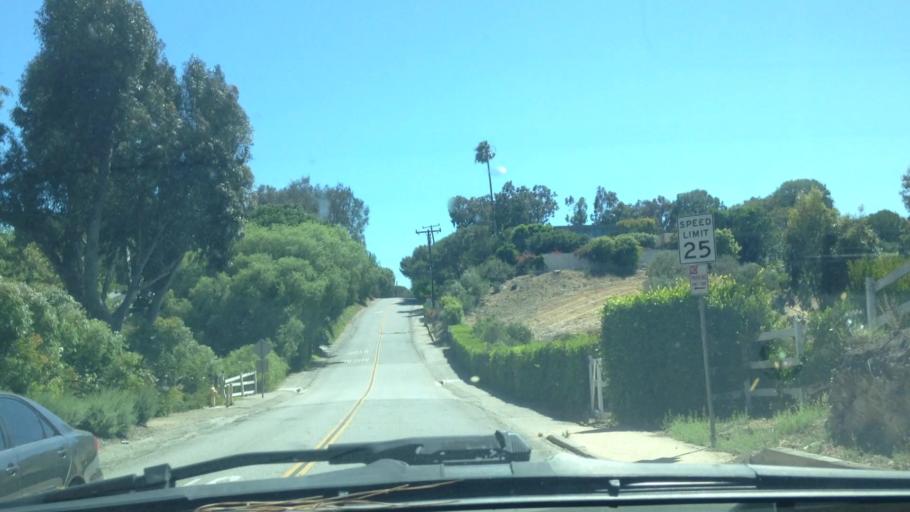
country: US
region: California
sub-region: Los Angeles County
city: Malibu
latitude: 34.0152
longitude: -118.7987
